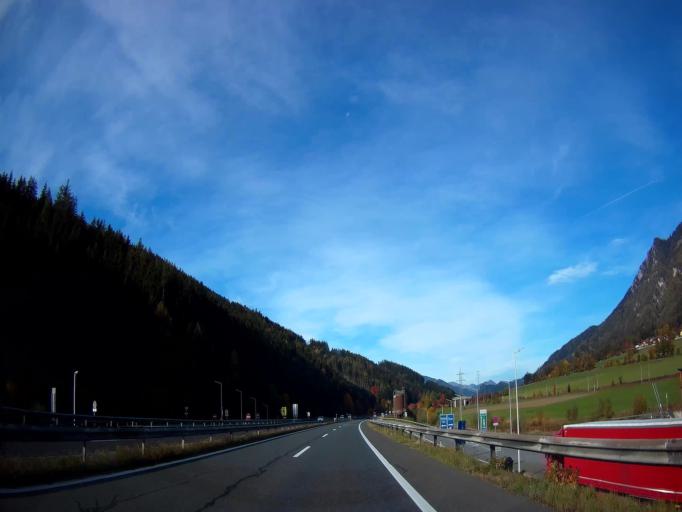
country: AT
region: Styria
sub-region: Politischer Bezirk Leoben
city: Kammern im Liesingtal
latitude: 47.3868
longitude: 14.8988
